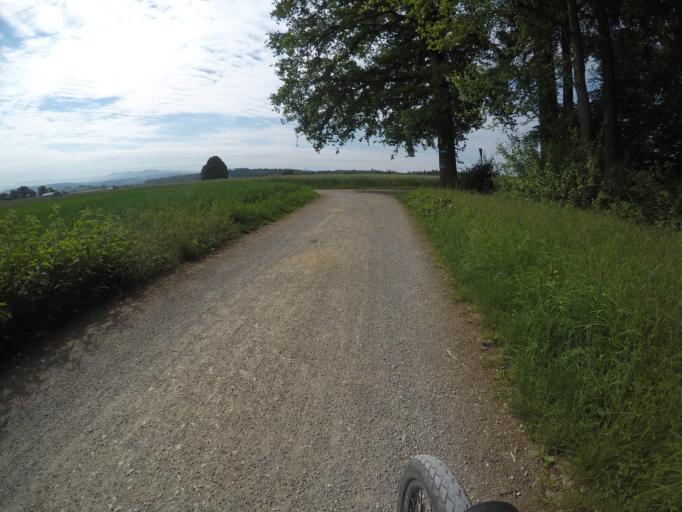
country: DE
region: Baden-Wuerttemberg
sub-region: Regierungsbezirk Stuttgart
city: Denkendorf
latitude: 48.6647
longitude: 9.3209
